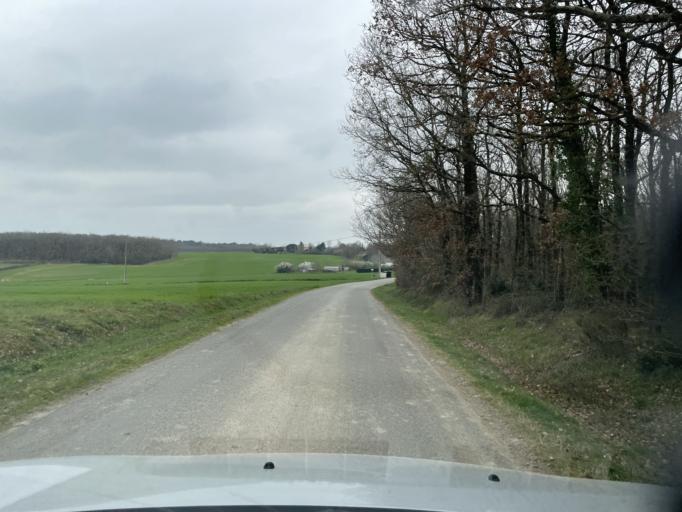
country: FR
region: Midi-Pyrenees
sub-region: Departement du Gers
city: Pujaudran
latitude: 43.6124
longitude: 1.1666
